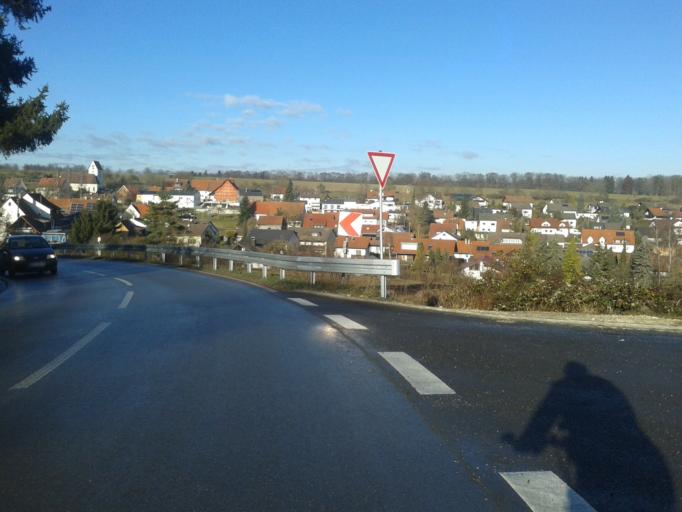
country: DE
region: Baden-Wuerttemberg
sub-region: Tuebingen Region
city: Erbach
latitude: 48.3951
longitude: 9.8640
